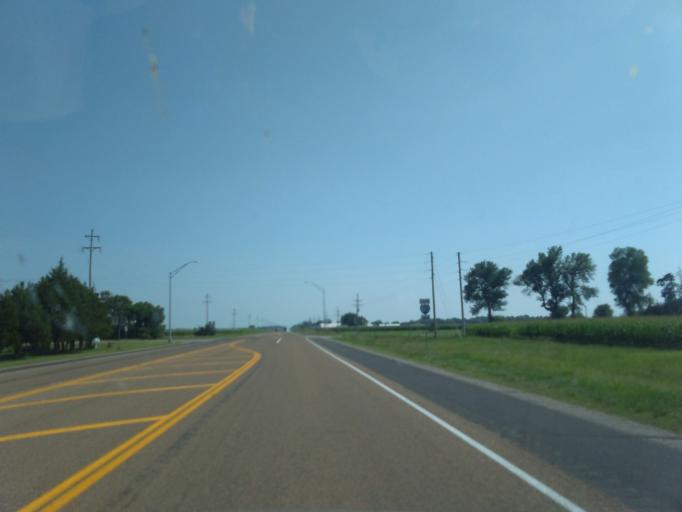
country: US
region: Nebraska
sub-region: Buffalo County
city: Kearney
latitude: 40.6420
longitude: -99.0849
